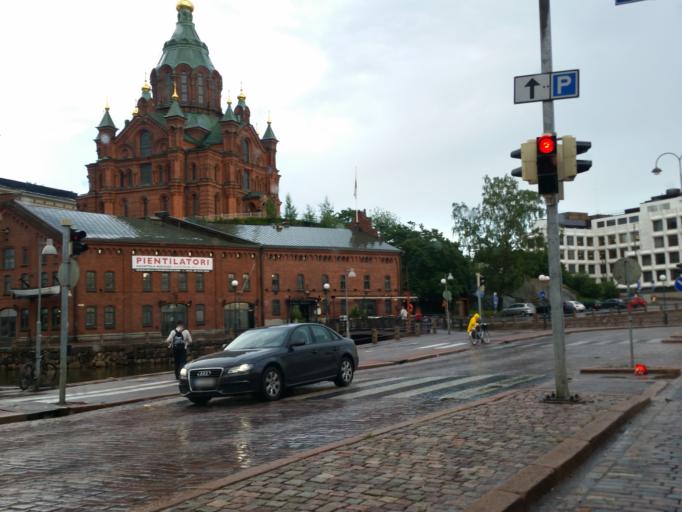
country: FI
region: Uusimaa
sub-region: Helsinki
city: Helsinki
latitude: 60.1695
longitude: 24.9584
